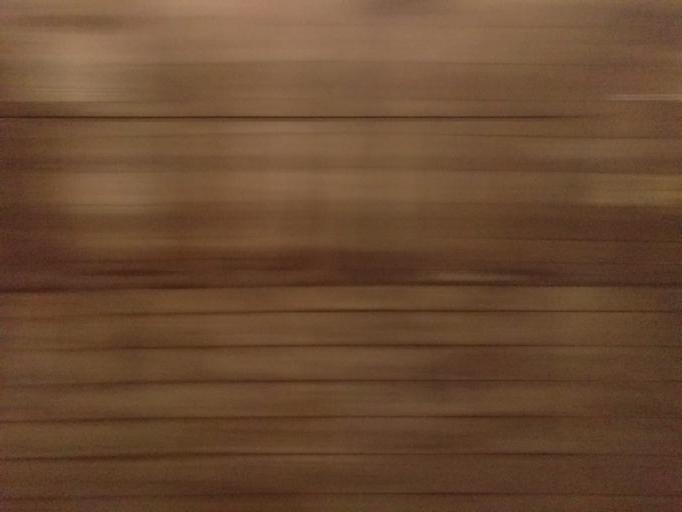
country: JP
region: Tokyo
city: Chofugaoka
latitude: 35.5962
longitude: 139.6072
